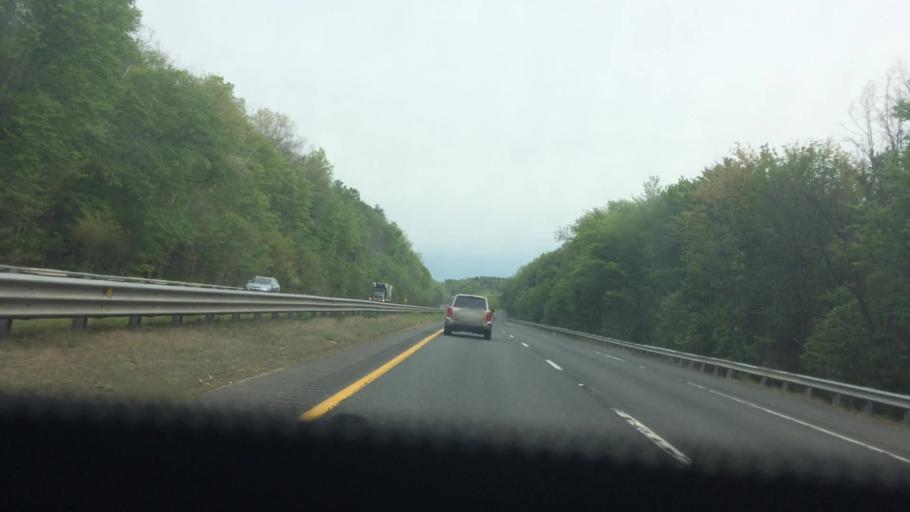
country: US
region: Massachusetts
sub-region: Worcester County
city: Fiskdale
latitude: 42.1426
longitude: -72.1378
